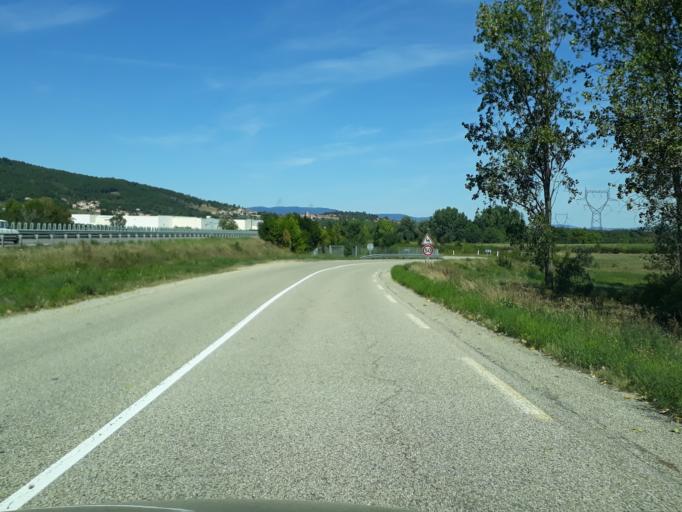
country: FR
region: Rhone-Alpes
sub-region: Departement de l'Ardeche
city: Peaugres
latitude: 45.2970
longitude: 4.7368
